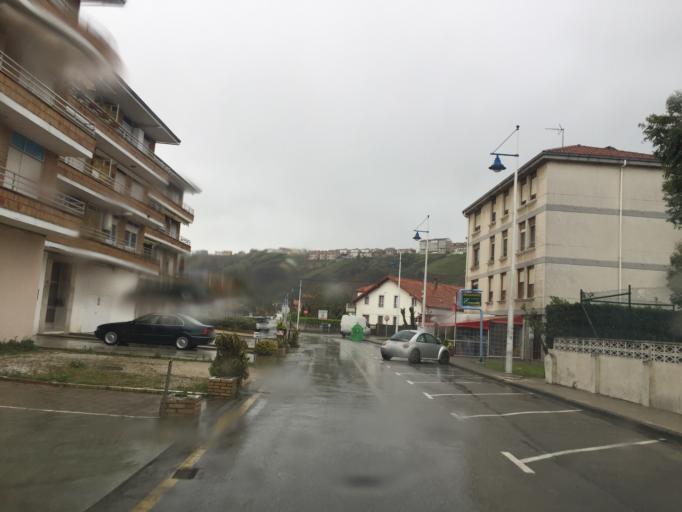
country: ES
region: Cantabria
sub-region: Provincia de Cantabria
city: Suances
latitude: 43.4303
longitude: -4.0373
